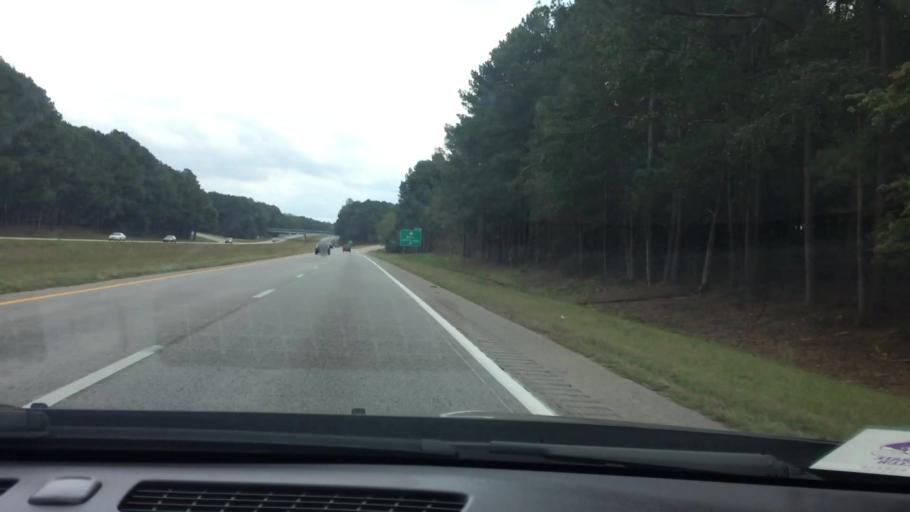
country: US
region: North Carolina
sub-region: Nash County
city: Spring Hope
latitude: 35.7876
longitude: -78.1244
